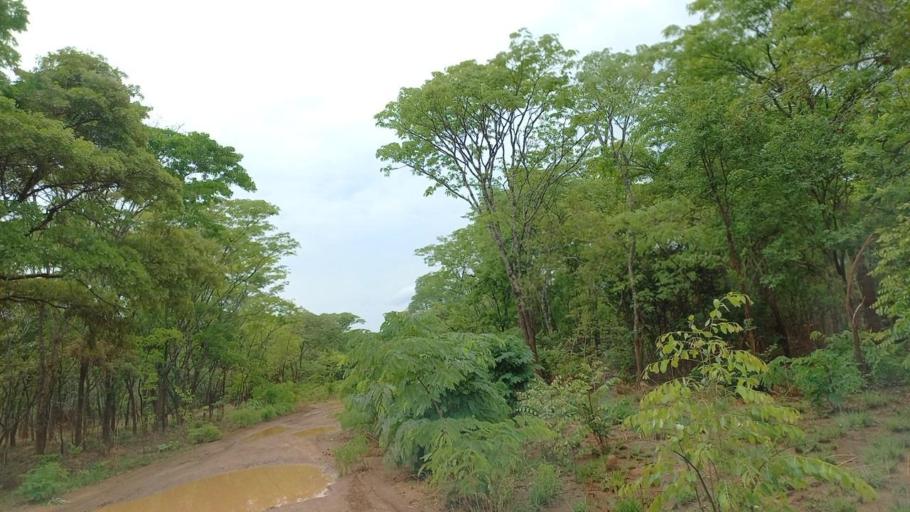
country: ZM
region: North-Western
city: Kalengwa
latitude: -13.5995
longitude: 24.9740
